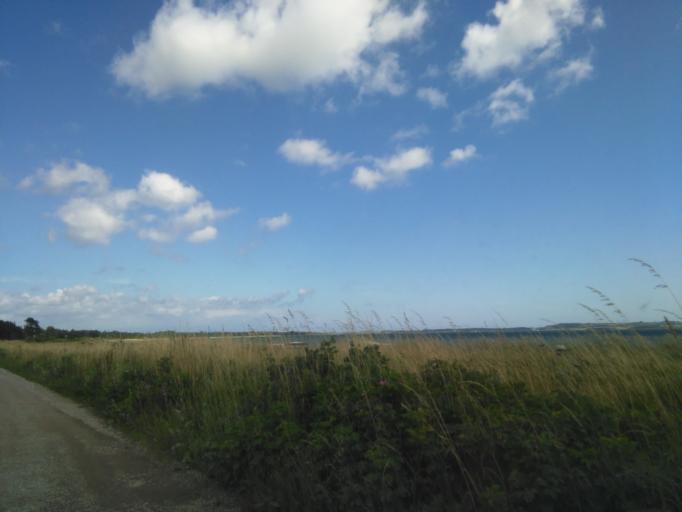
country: DK
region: Central Jutland
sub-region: Syddjurs Kommune
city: Ronde
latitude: 56.1819
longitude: 10.4507
